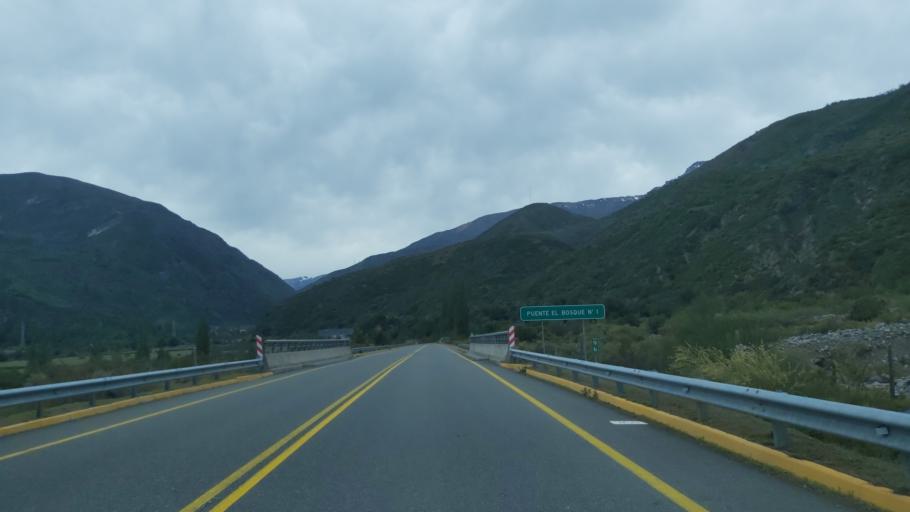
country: CL
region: Maule
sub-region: Provincia de Linares
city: Colbun
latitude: -35.8156
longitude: -70.8446
